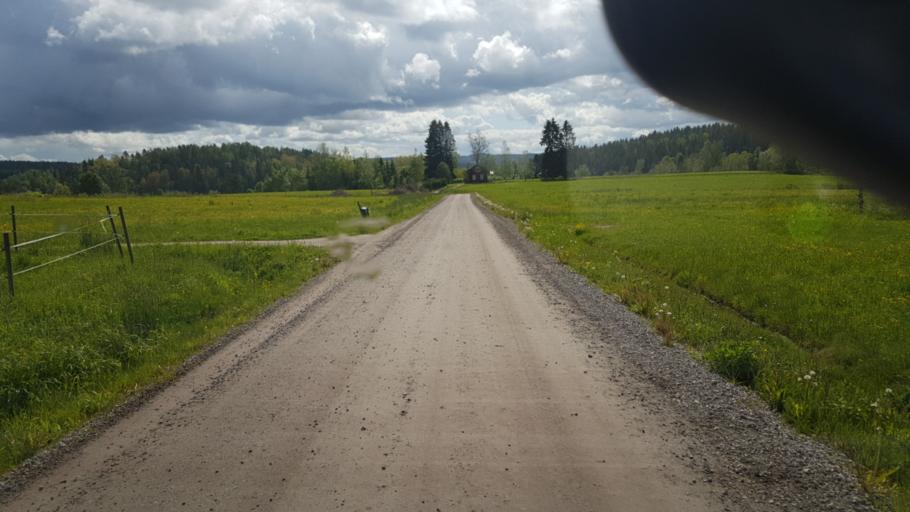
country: NO
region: Ostfold
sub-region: Romskog
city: Romskog
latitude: 59.7000
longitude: 12.0636
